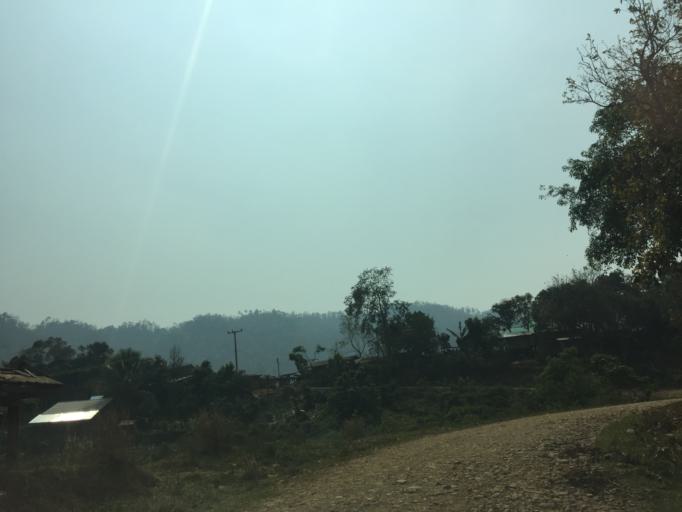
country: TH
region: Phayao
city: Phu Sang
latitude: 19.5674
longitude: 100.5254
